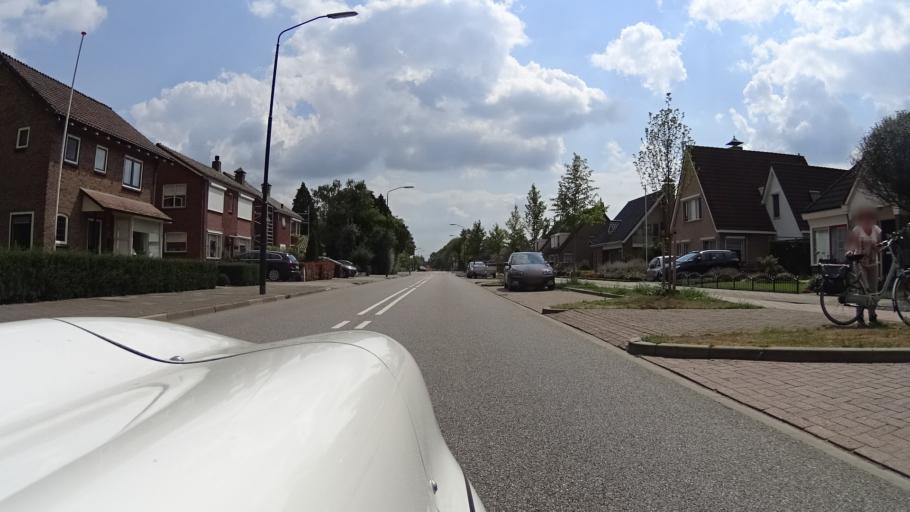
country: NL
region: North Brabant
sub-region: Gemeente Woudrichem
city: Woudrichem
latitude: 51.7905
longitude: 5.0291
